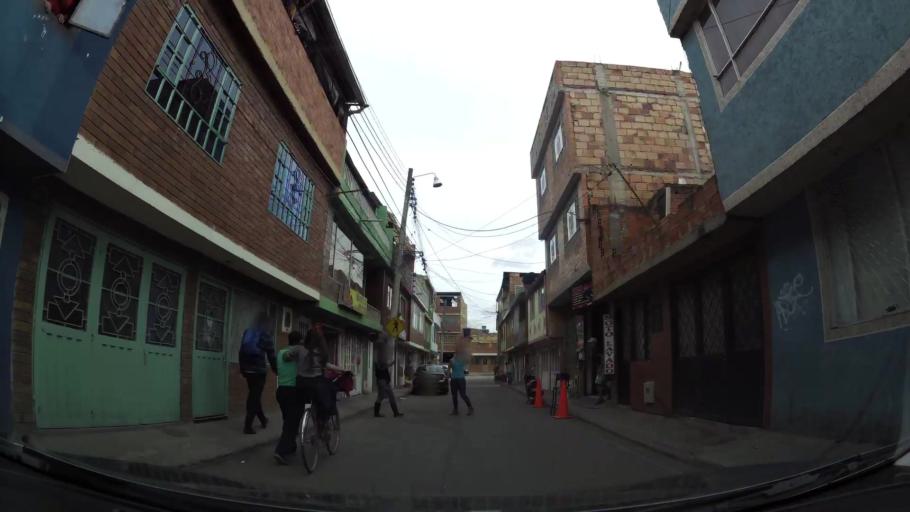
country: CO
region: Cundinamarca
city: Funza
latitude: 4.7105
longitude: -74.2186
